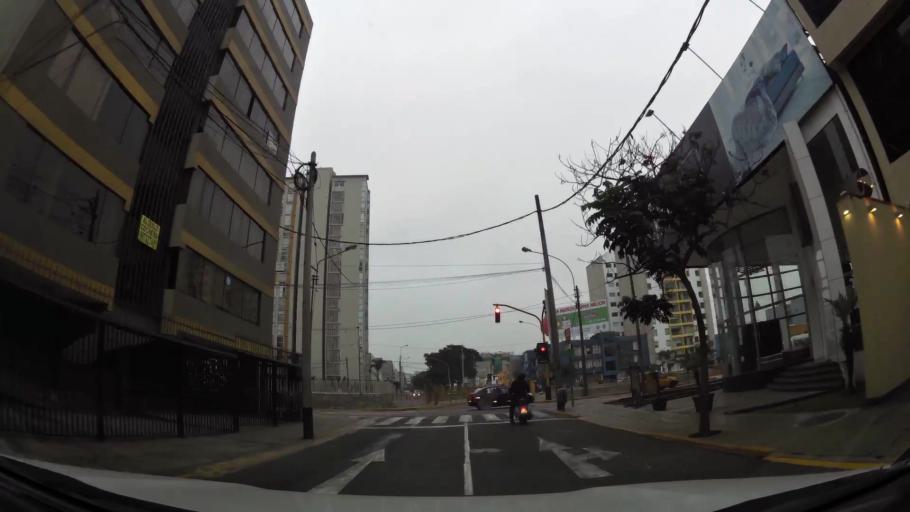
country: PE
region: Lima
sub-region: Lima
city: San Isidro
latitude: -12.1221
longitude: -77.0255
